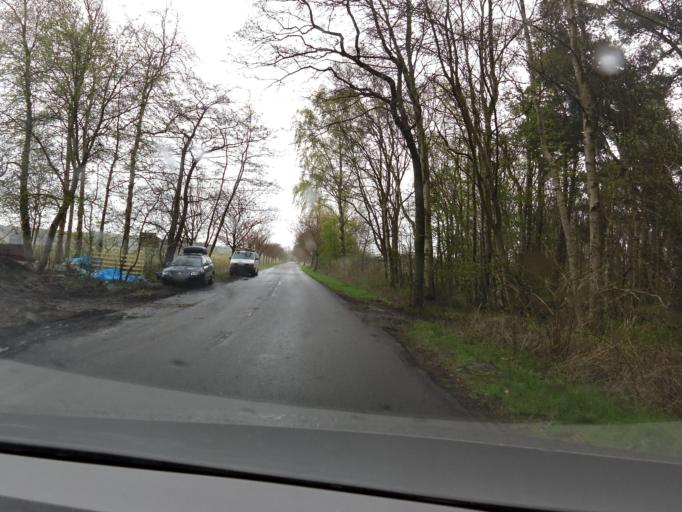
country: DE
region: Mecklenburg-Vorpommern
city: Zingst
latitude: 54.4378
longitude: 12.7235
